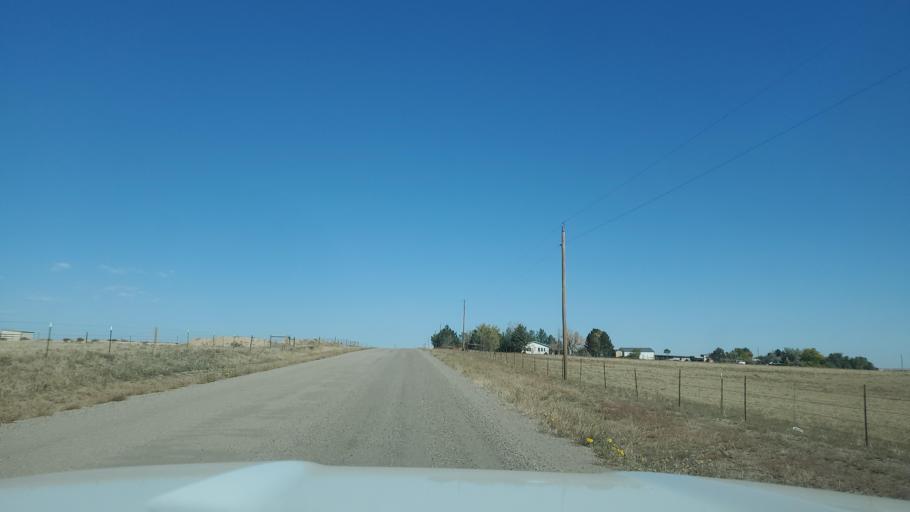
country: US
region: Colorado
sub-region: Adams County
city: Bennett
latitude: 39.7692
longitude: -104.3769
